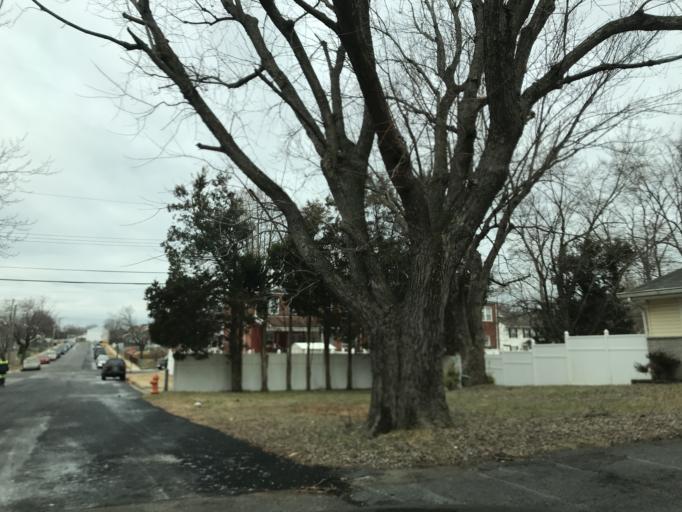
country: US
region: Maryland
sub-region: Baltimore County
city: Middle River
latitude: 39.3382
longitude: -76.4415
